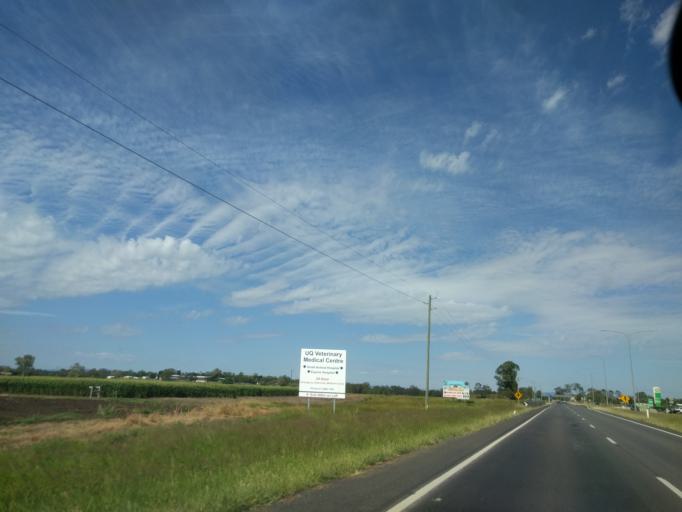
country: AU
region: Queensland
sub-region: Lockyer Valley
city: Gatton
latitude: -27.5446
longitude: 152.3470
